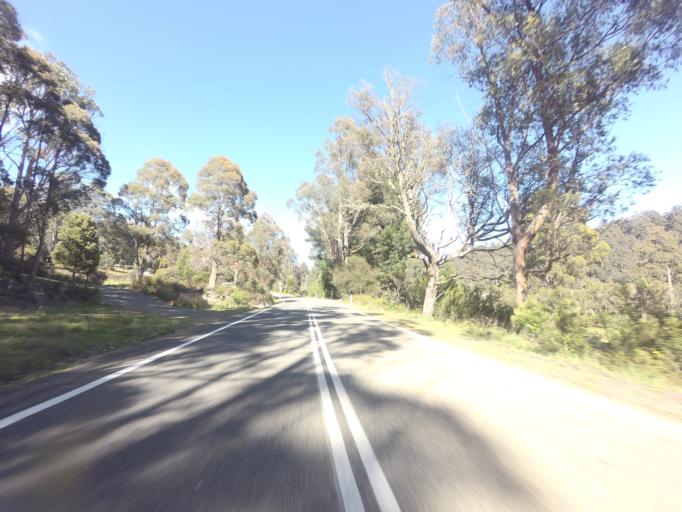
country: AU
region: Tasmania
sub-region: Derwent Valley
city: New Norfolk
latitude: -42.7053
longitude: 146.7125
